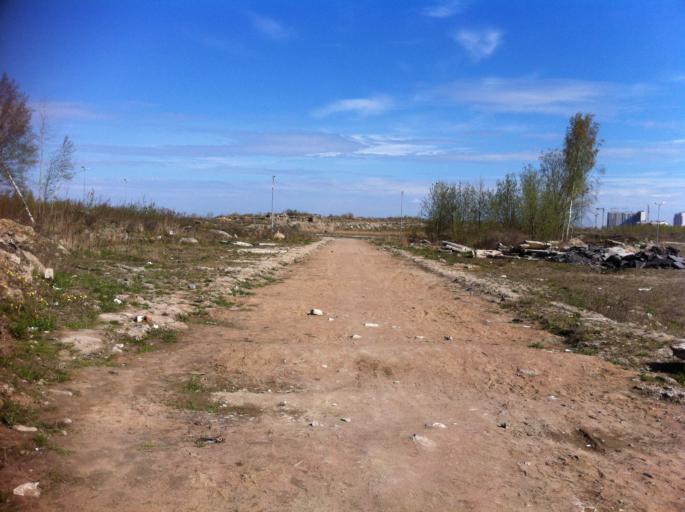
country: RU
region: St.-Petersburg
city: Sosnovaya Polyana
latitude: 59.8563
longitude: 30.1428
